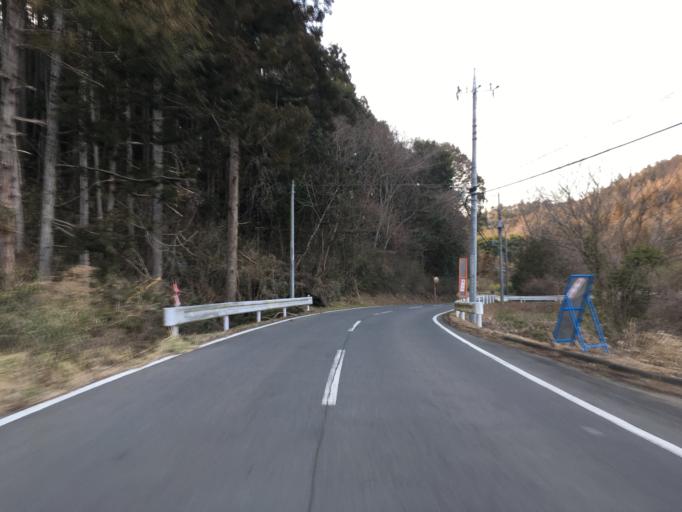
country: JP
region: Ibaraki
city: Daigo
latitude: 36.8060
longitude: 140.3779
